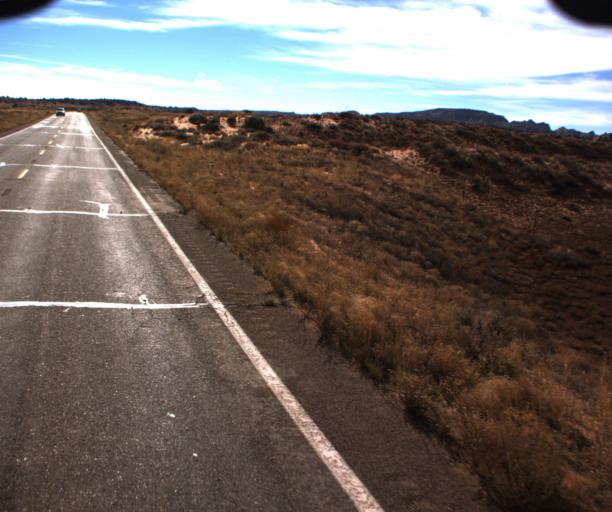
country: US
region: Arizona
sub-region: Coconino County
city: Kaibito
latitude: 36.5876
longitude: -111.1531
